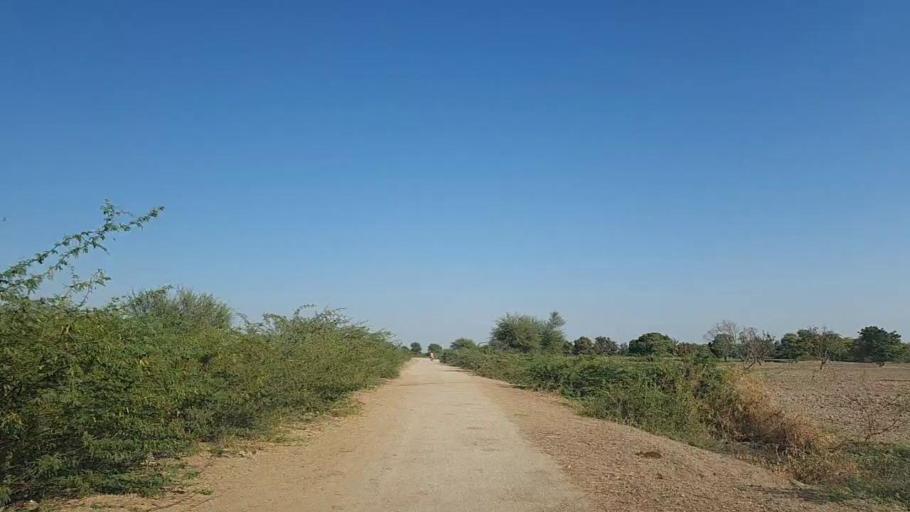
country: PK
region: Sindh
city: Samaro
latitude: 25.2490
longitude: 69.4860
